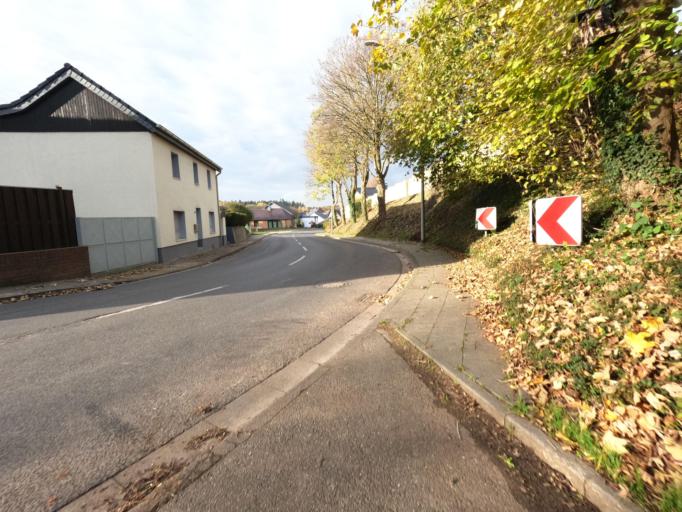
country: DE
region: North Rhine-Westphalia
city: Geilenkirchen
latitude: 50.9769
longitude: 6.1511
